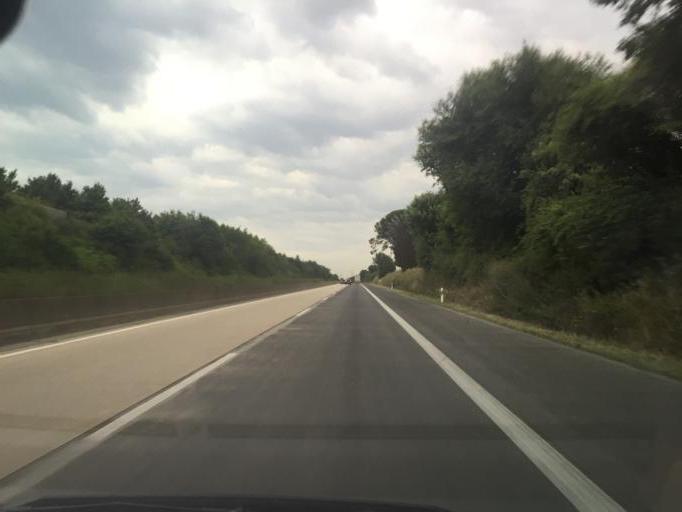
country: DE
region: North Rhine-Westphalia
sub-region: Regierungsbezirk Koln
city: Bedburg
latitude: 50.9807
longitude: 6.5576
